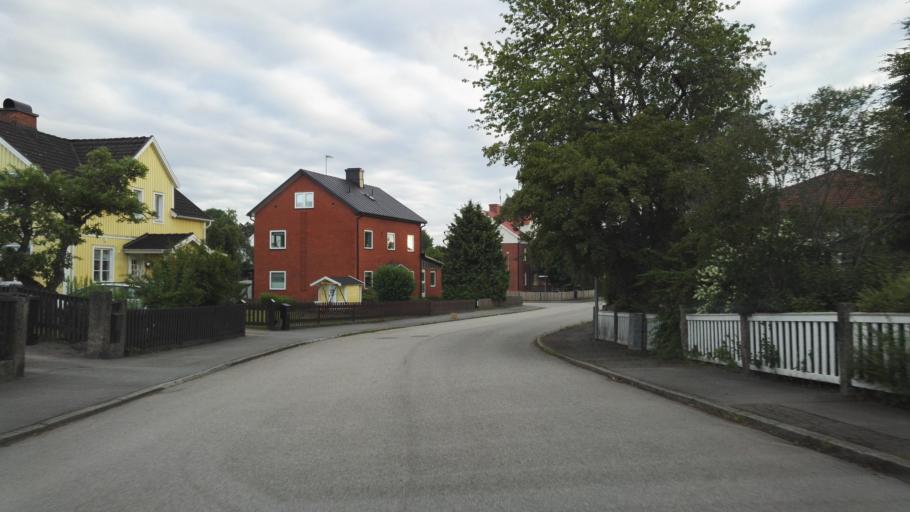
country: SE
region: Kronoberg
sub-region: Vaxjo Kommun
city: Vaexjoe
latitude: 56.8744
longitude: 14.7918
